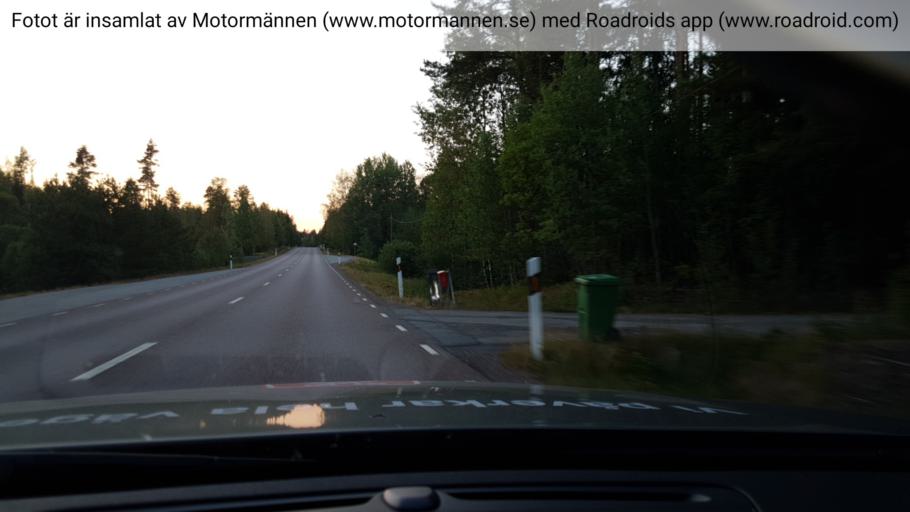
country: SE
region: Uppsala
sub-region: Heby Kommun
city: OEstervala
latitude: 60.0622
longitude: 17.2210
